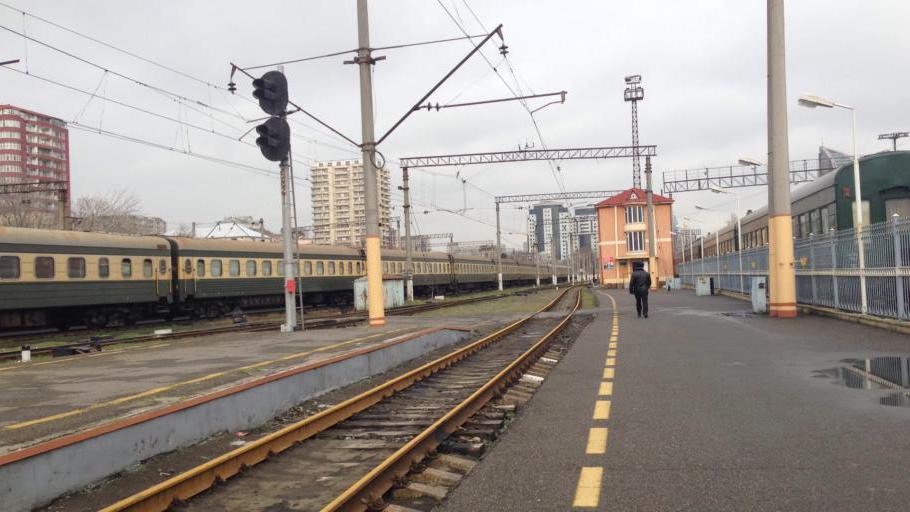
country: AZ
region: Baki
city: Baku
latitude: 40.3837
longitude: 49.8545
